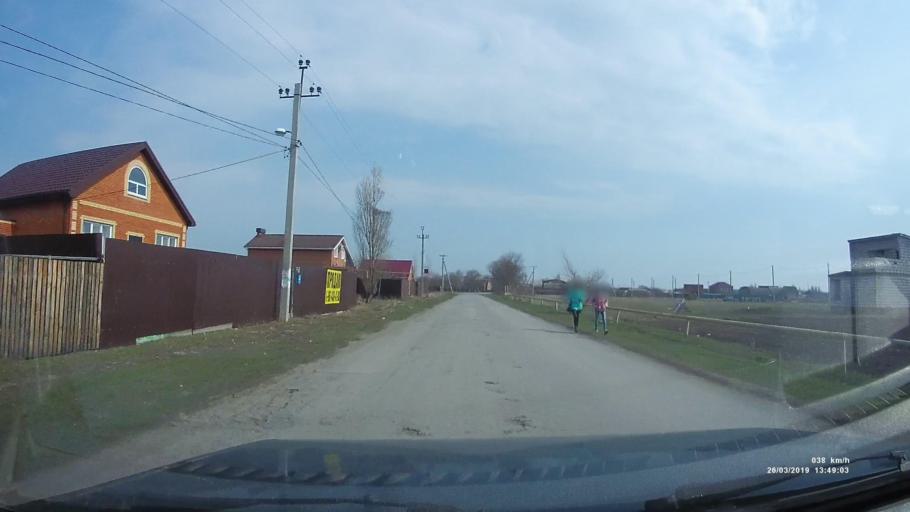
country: RU
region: Rostov
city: Novobessergenovka
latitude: 47.1913
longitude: 38.8633
